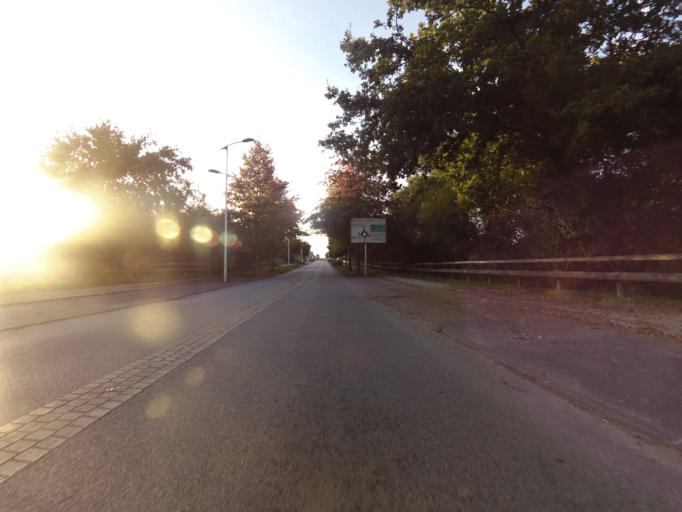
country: FR
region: Brittany
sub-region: Departement du Morbihan
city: Theix
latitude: 47.6289
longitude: -2.6464
